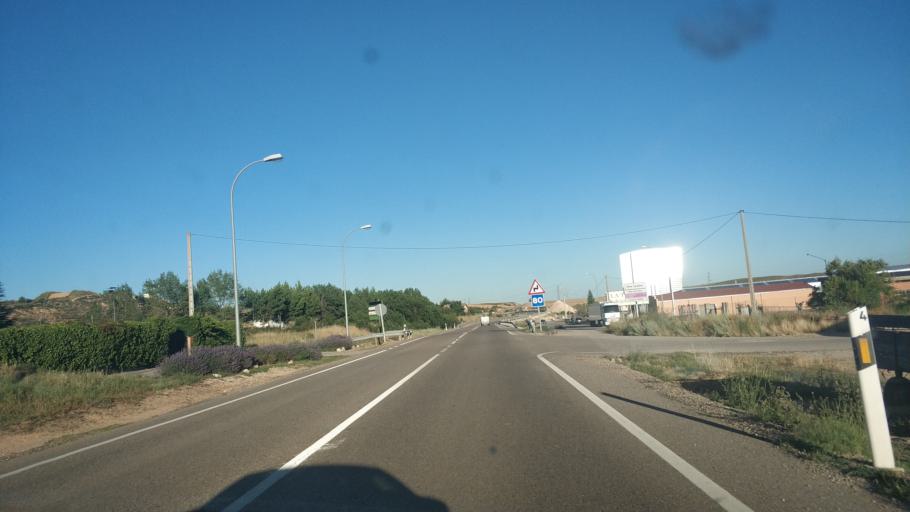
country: ES
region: Castille and Leon
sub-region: Provincia de Soria
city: San Esteban de Gormaz
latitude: 41.5675
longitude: -3.1890
